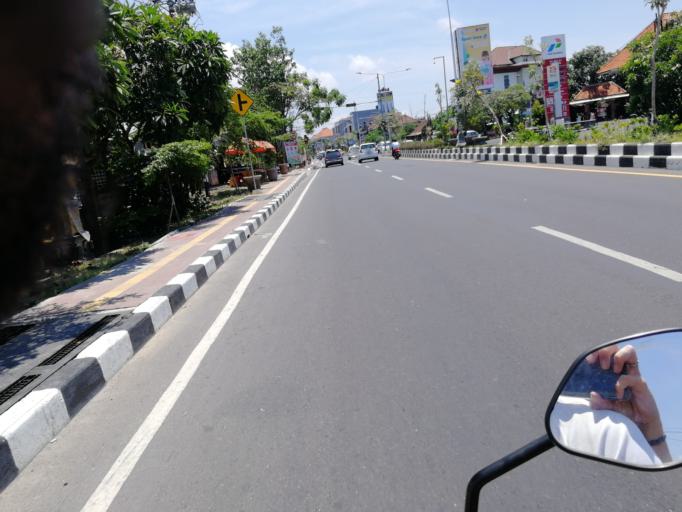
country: ID
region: Bali
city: Kuta
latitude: -8.6961
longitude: 115.1866
